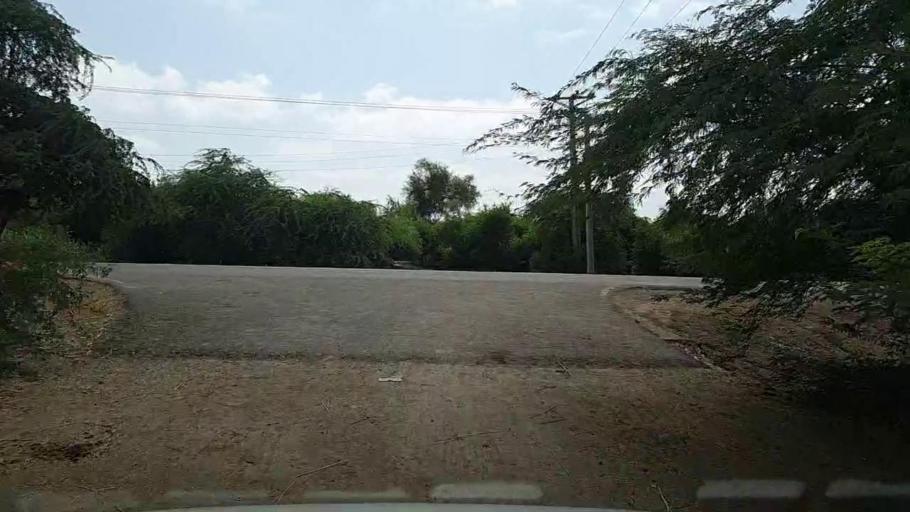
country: PK
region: Sindh
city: Talhar
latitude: 24.8904
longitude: 68.6955
